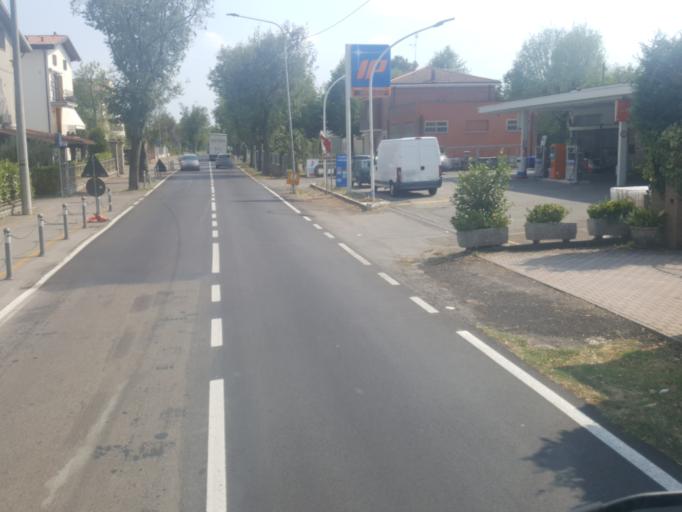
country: IT
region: Emilia-Romagna
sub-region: Provincia di Modena
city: Gaggio
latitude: 44.6354
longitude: 11.0110
